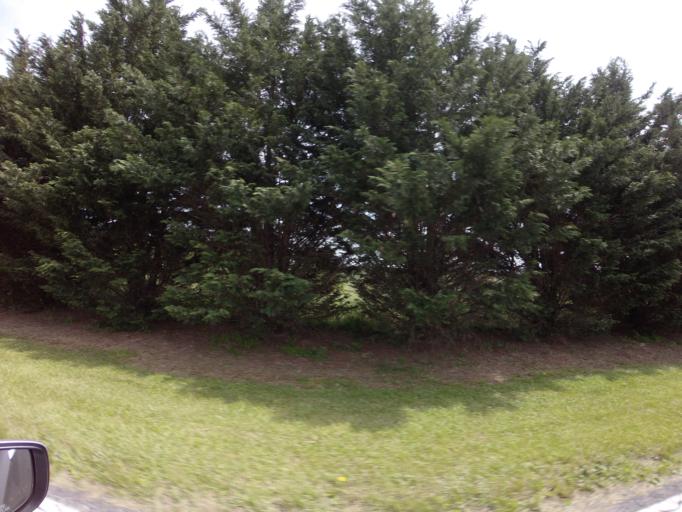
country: US
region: Maryland
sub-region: Carroll County
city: New Windsor
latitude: 39.4925
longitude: -77.1354
